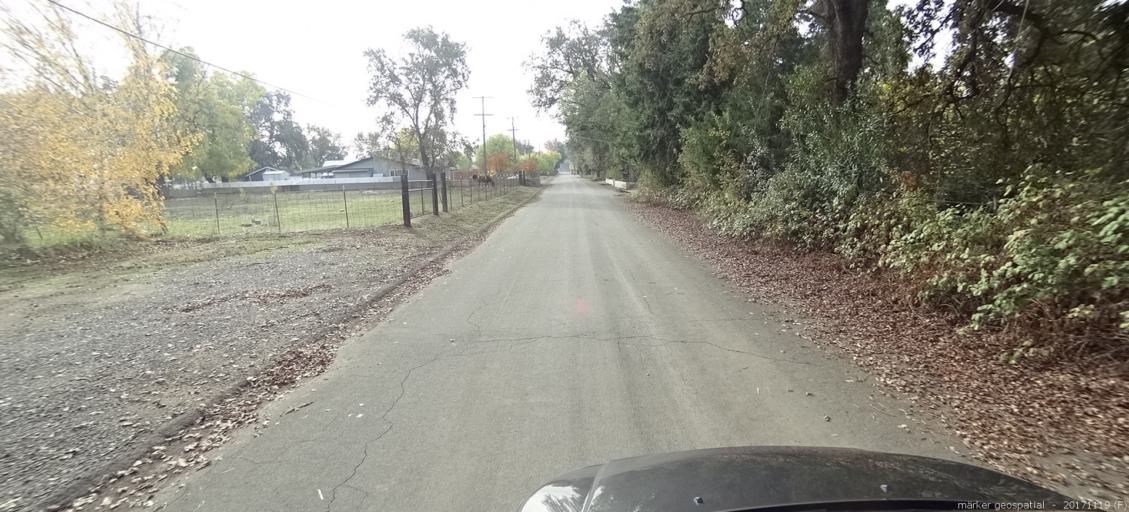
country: US
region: California
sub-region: Shasta County
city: Redding
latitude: 40.5260
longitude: -122.3394
